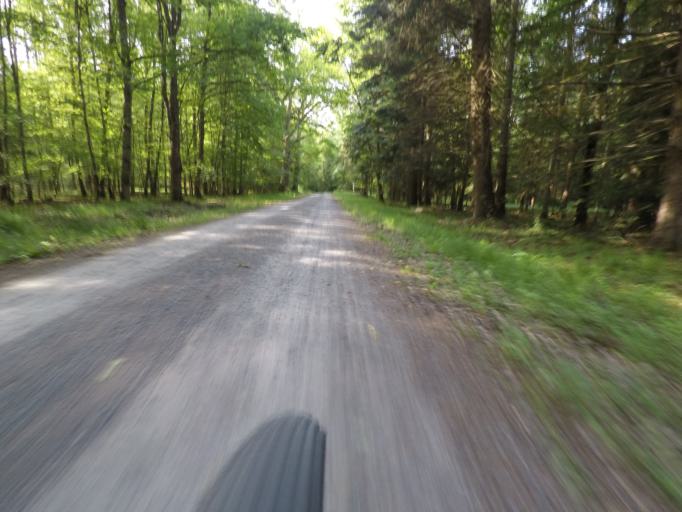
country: DE
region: Baden-Wuerttemberg
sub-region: Regierungsbezirk Stuttgart
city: Weil im Schonbuch
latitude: 48.5788
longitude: 9.0594
